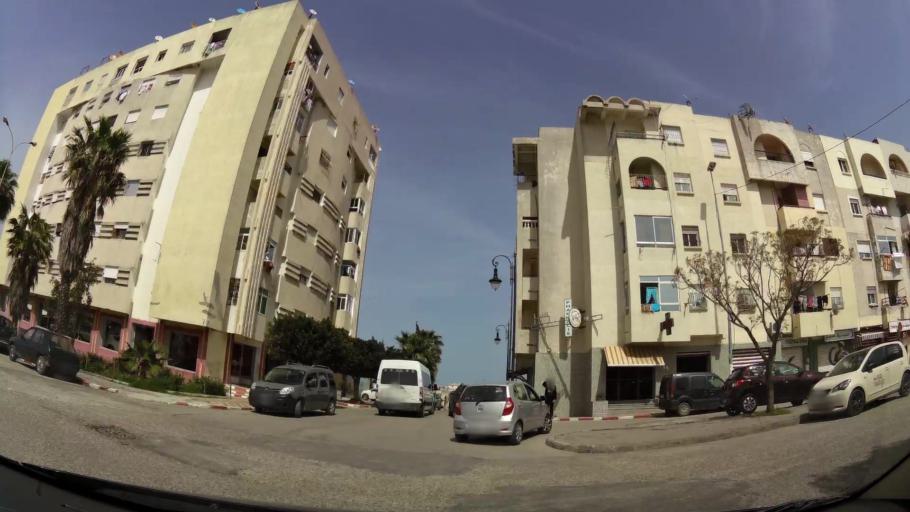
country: MA
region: Tanger-Tetouan
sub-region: Tanger-Assilah
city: Tangier
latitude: 35.7499
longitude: -5.8342
